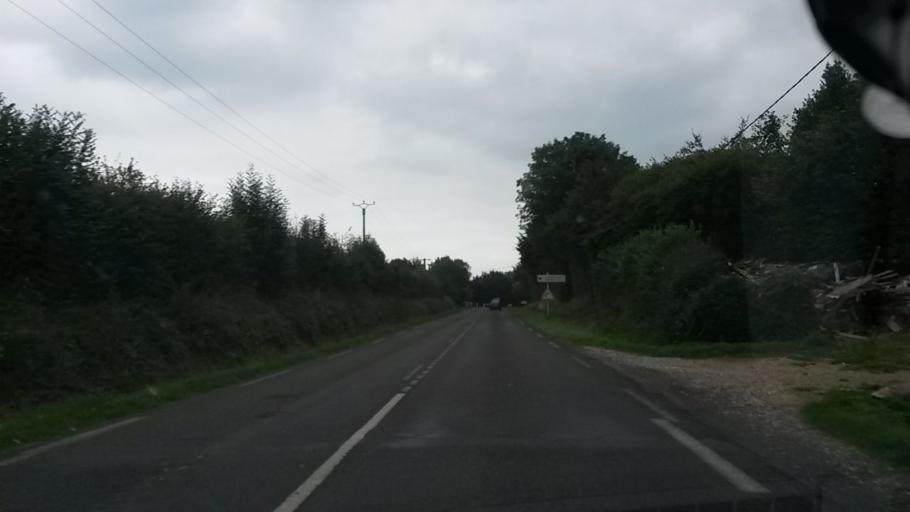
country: FR
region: Haute-Normandie
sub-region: Departement de la Seine-Maritime
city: Gaillefontaine
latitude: 49.6401
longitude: 1.6133
